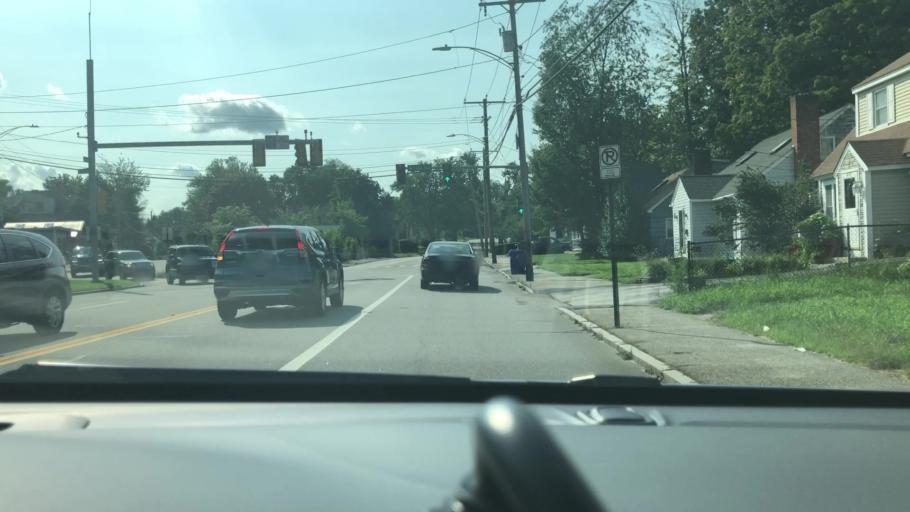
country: US
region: New Hampshire
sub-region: Hillsborough County
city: Manchester
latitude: 42.9879
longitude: -71.4290
